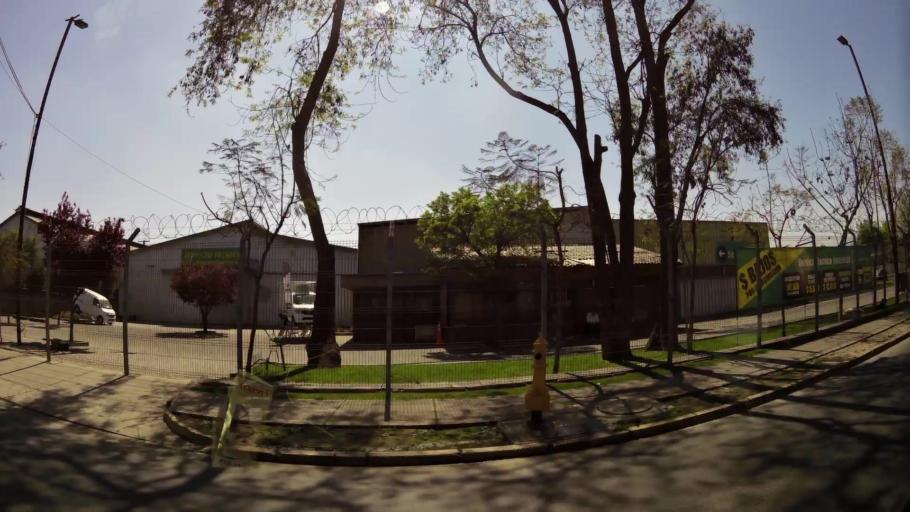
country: CL
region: Santiago Metropolitan
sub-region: Provincia de Santiago
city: Lo Prado
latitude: -33.3679
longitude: -70.7068
